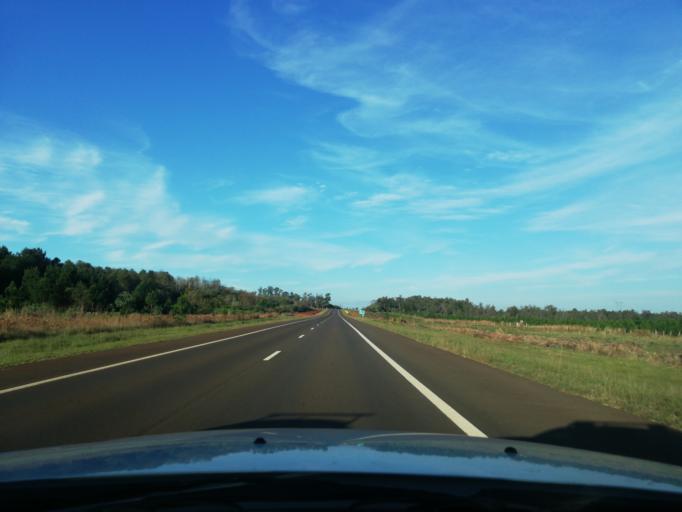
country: AR
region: Misiones
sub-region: Departamento de Capital
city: Posadas
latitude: -27.4608
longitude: -55.9929
